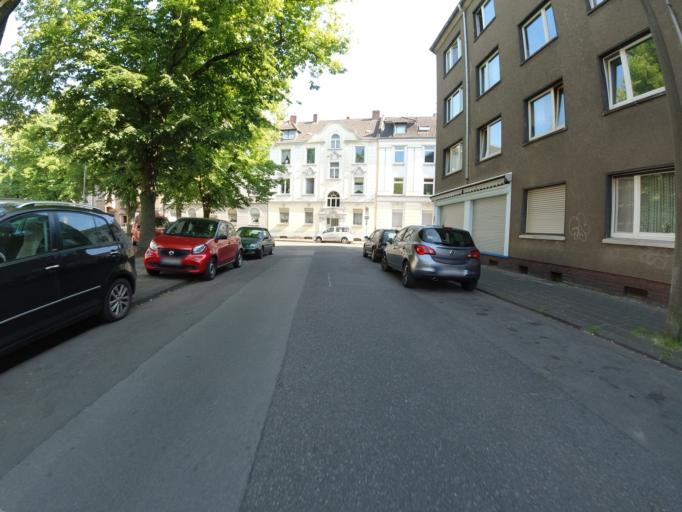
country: DE
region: North Rhine-Westphalia
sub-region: Regierungsbezirk Dusseldorf
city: Hochfeld
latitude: 51.4086
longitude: 6.7198
